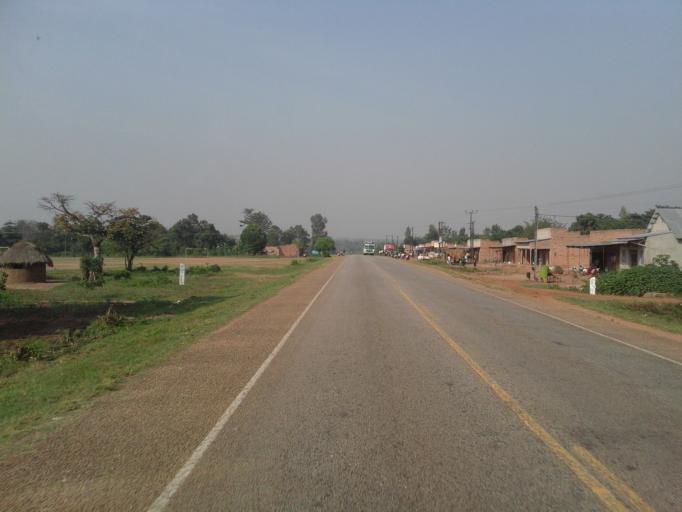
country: UG
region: Eastern Region
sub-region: Mbale District
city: Mbale
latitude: 1.0525
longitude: 34.0507
